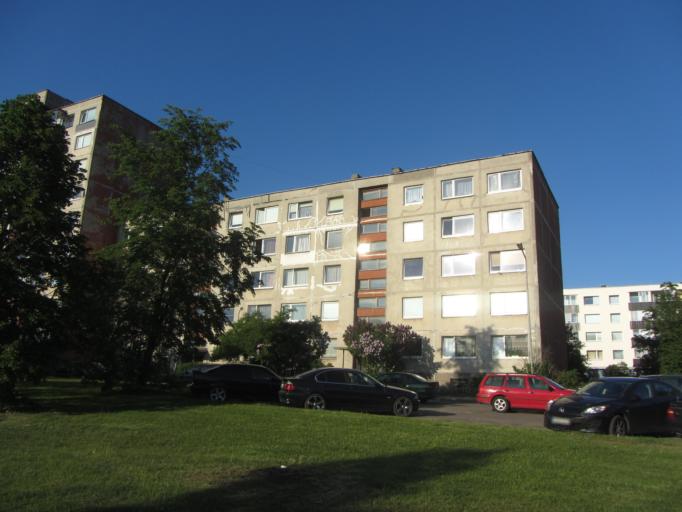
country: LT
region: Vilnius County
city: Seskine
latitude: 54.7271
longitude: 25.2691
